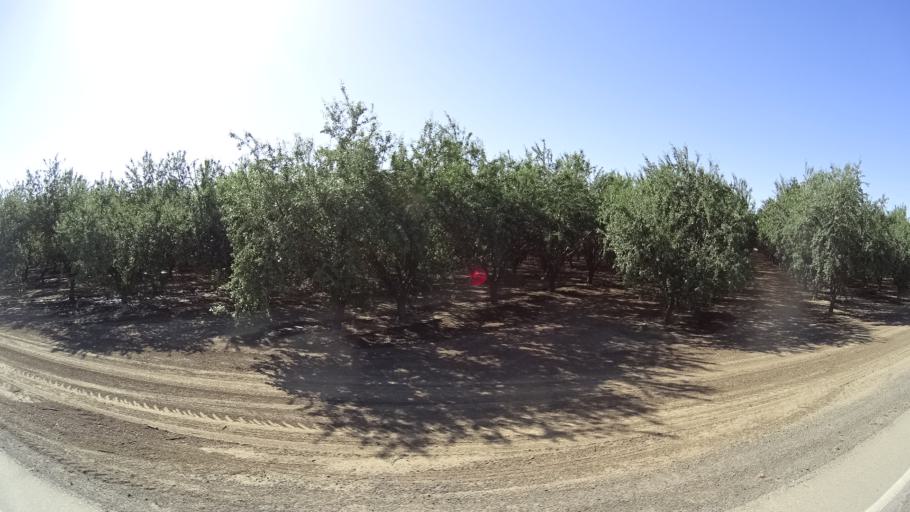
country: US
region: California
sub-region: Fresno County
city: Huron
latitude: 36.1123
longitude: -120.0438
